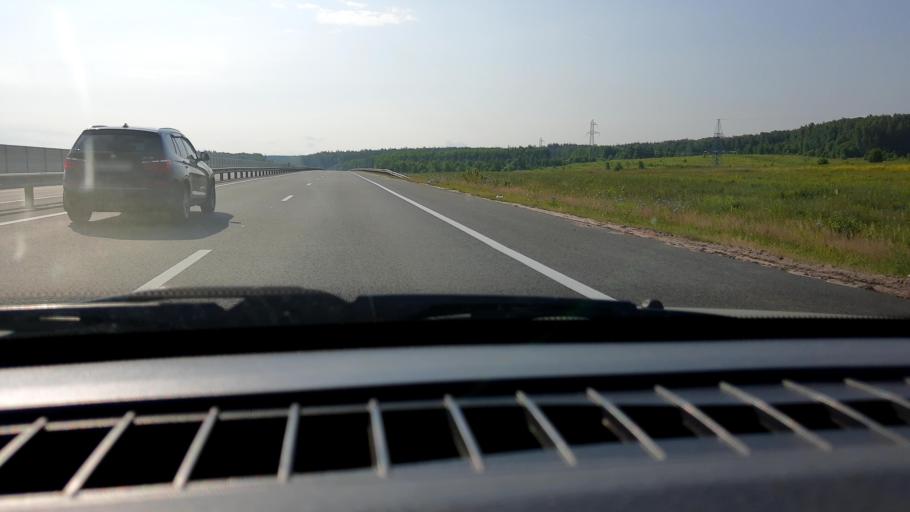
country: RU
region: Nizjnij Novgorod
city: Burevestnik
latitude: 56.1115
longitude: 43.9714
